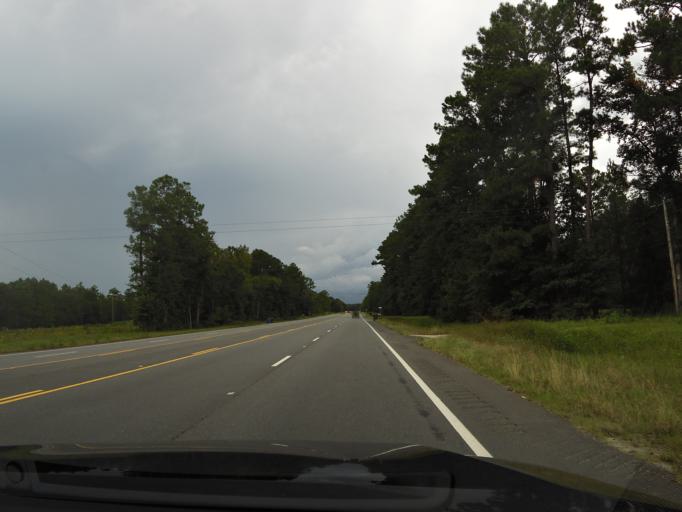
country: US
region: Georgia
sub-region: Glynn County
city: Dock Junction
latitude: 31.2885
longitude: -81.5671
